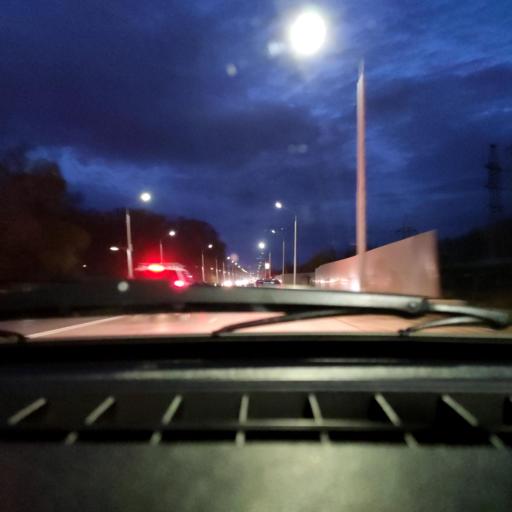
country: RU
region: Bashkortostan
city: Ufa
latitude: 54.7885
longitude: 56.1154
